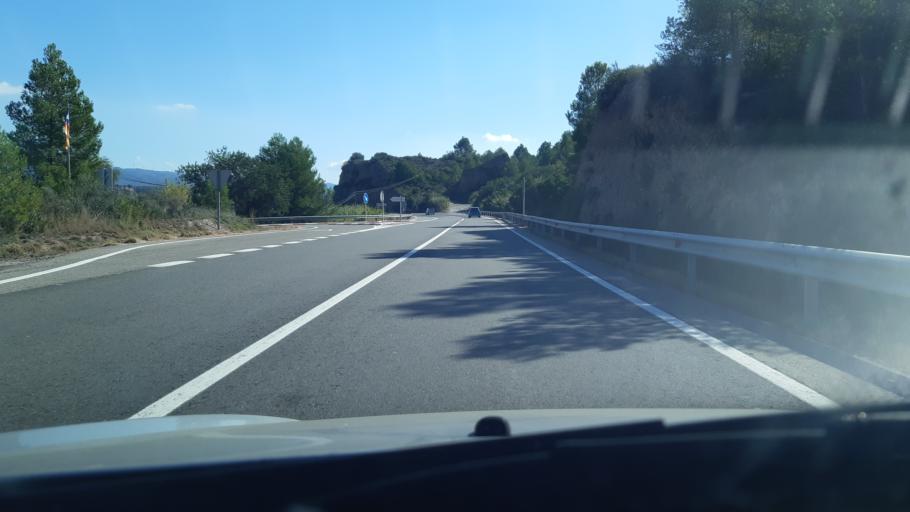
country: ES
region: Catalonia
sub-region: Provincia de Tarragona
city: Tivenys
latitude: 40.8995
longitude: 0.4844
